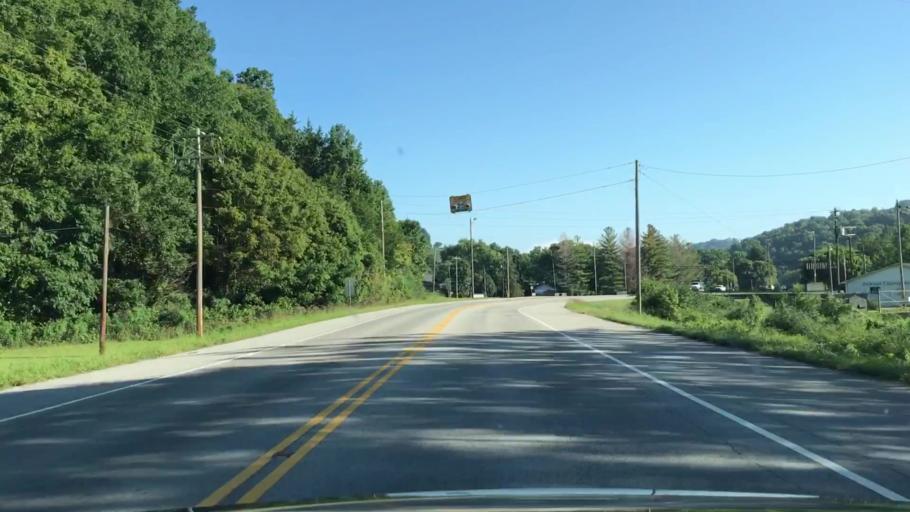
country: US
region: Tennessee
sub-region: Jackson County
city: Gainesboro
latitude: 36.3475
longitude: -85.6582
